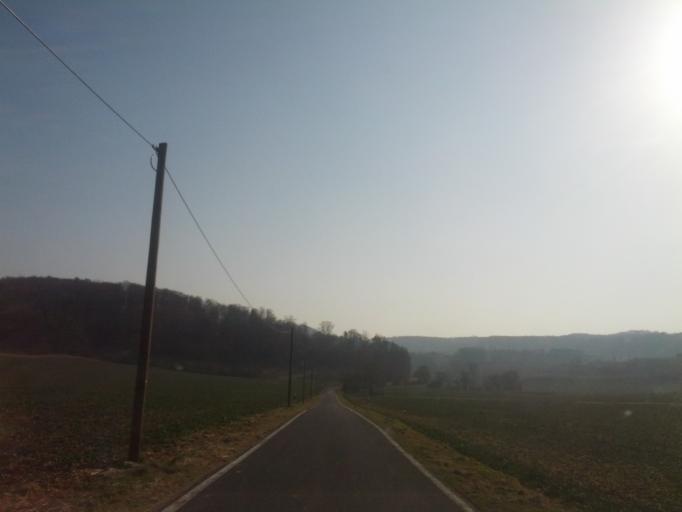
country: DE
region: Thuringia
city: Ifta
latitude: 51.0809
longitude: 10.1646
